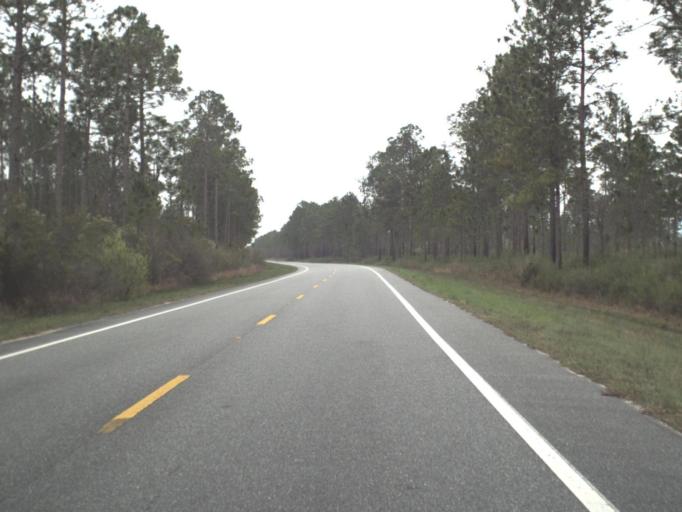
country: US
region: Florida
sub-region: Franklin County
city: Apalachicola
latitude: 29.8974
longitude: -84.9780
